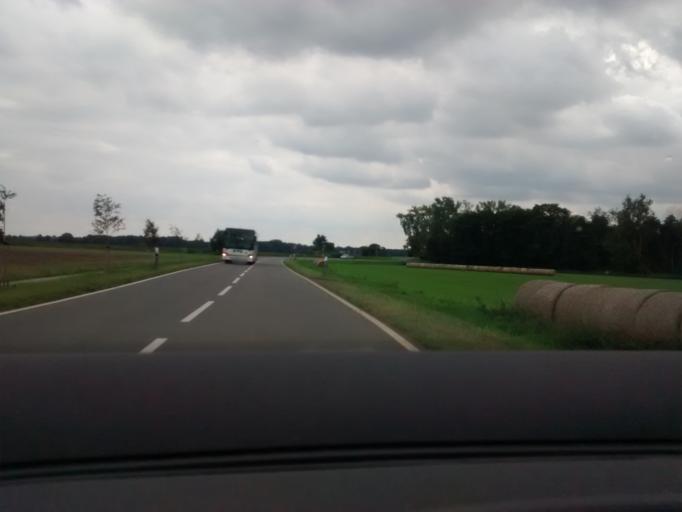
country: DE
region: Lower Saxony
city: Scharnebeck
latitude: 53.3210
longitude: 10.5047
